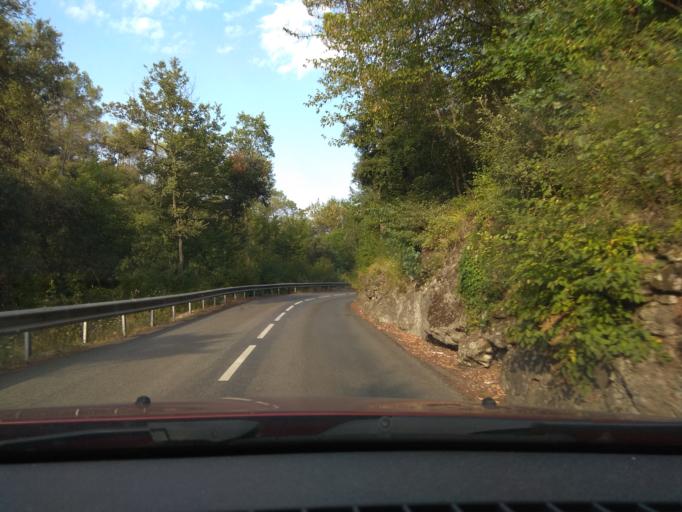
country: FR
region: Provence-Alpes-Cote d'Azur
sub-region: Departement des Alpes-Maritimes
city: Tourrettes-sur-Loup
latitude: 43.6823
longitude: 7.0535
